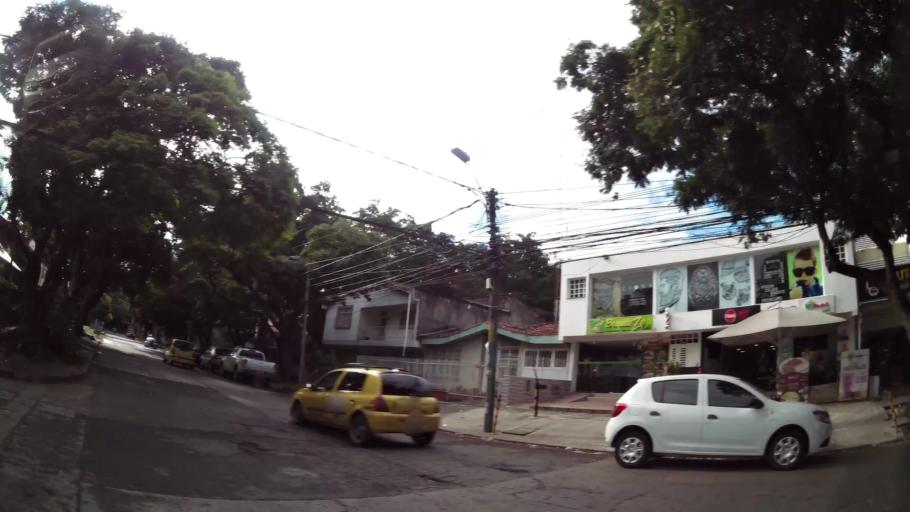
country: CO
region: Valle del Cauca
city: Cali
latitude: 3.4836
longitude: -76.5225
